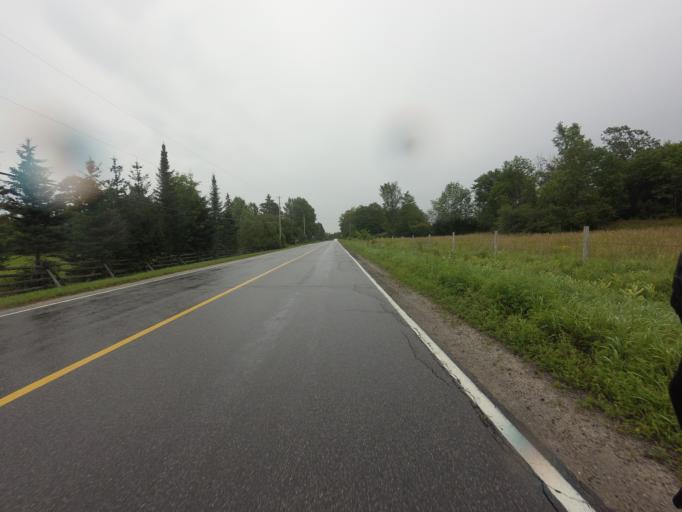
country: CA
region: Ontario
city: Perth
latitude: 44.9532
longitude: -76.4022
